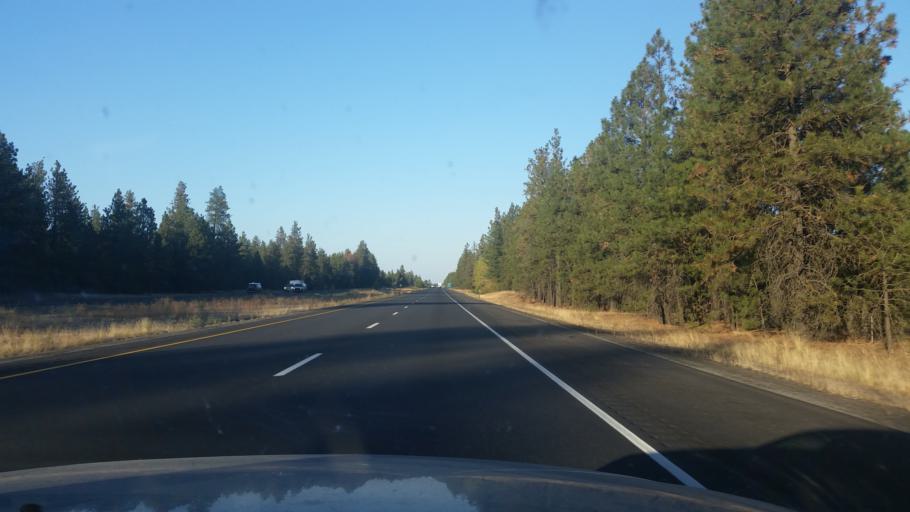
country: US
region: Washington
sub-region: Spokane County
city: Medical Lake
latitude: 47.4856
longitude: -117.7182
